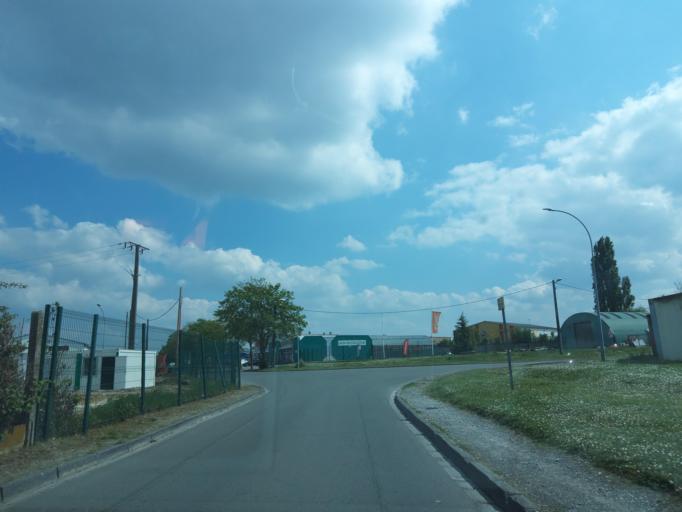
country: FR
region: Picardie
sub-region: Departement de l'Aisne
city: Laon
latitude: 49.5773
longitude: 3.6423
